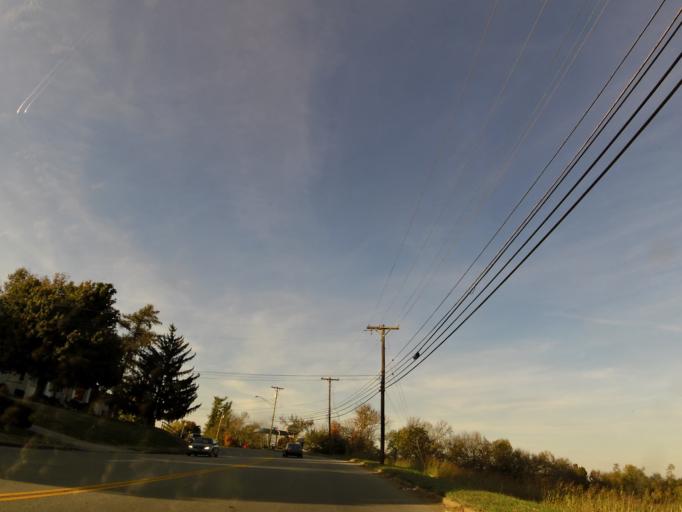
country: US
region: Kentucky
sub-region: Garrard County
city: Lancaster
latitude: 37.6276
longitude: -84.5792
